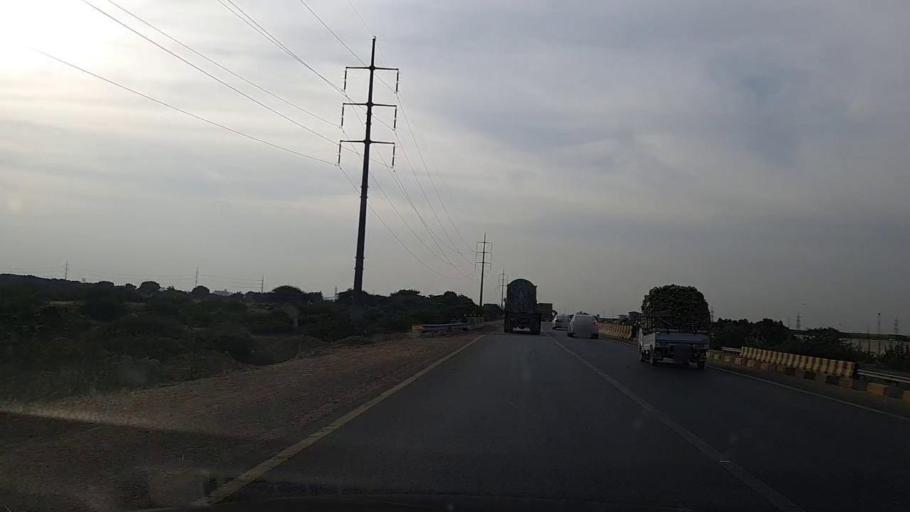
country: PK
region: Sindh
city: Gharo
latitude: 24.8372
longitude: 67.4498
